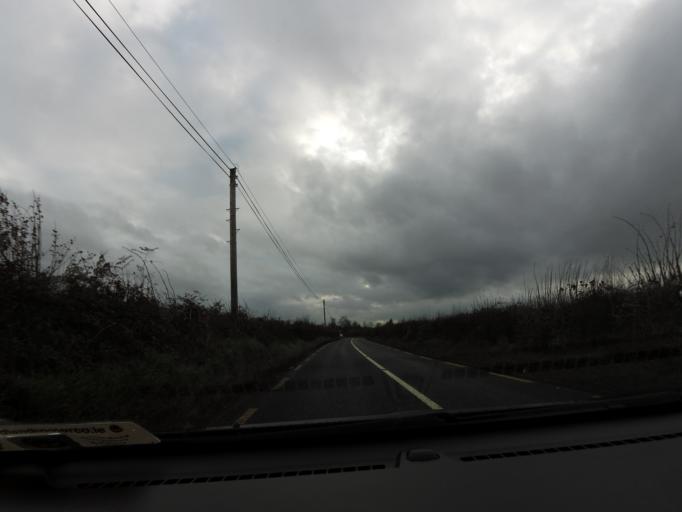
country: IE
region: Leinster
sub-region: Kilkenny
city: Kilkenny
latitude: 52.7120
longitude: -7.2834
